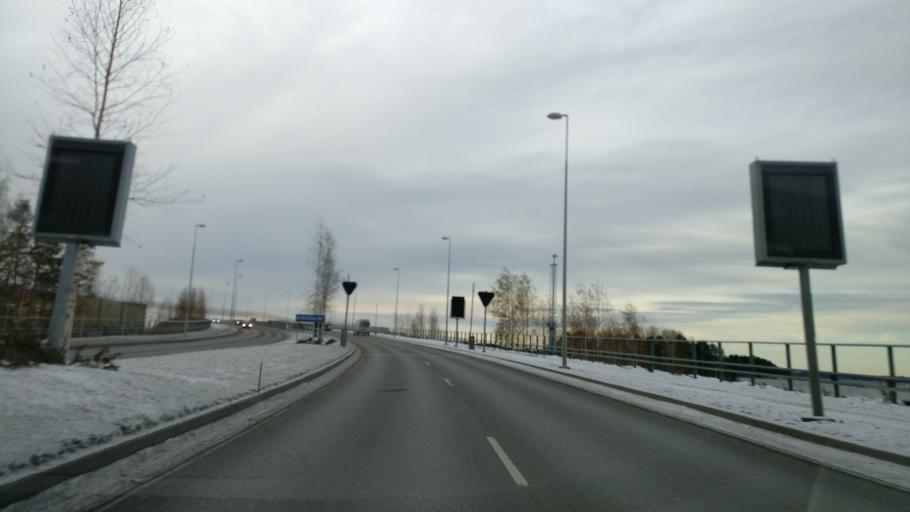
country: FI
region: Southern Savonia
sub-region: Savonlinna
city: Savonlinna
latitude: 61.8705
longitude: 28.9151
